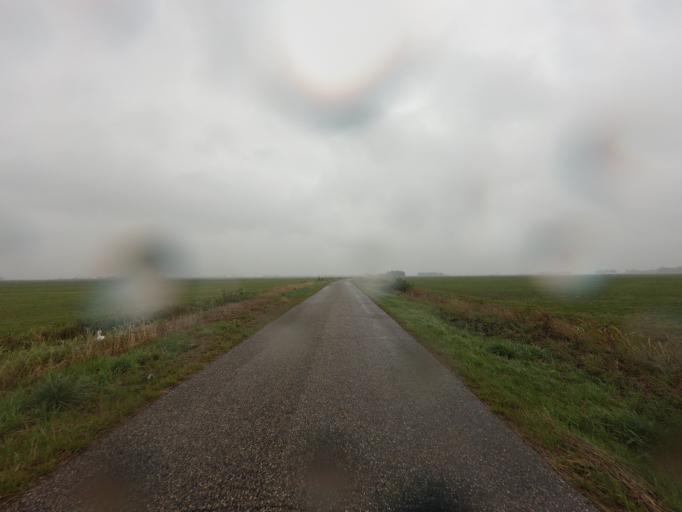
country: NL
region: Friesland
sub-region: Gemeente Boarnsterhim
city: Aldeboarn
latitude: 53.0755
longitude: 5.9301
